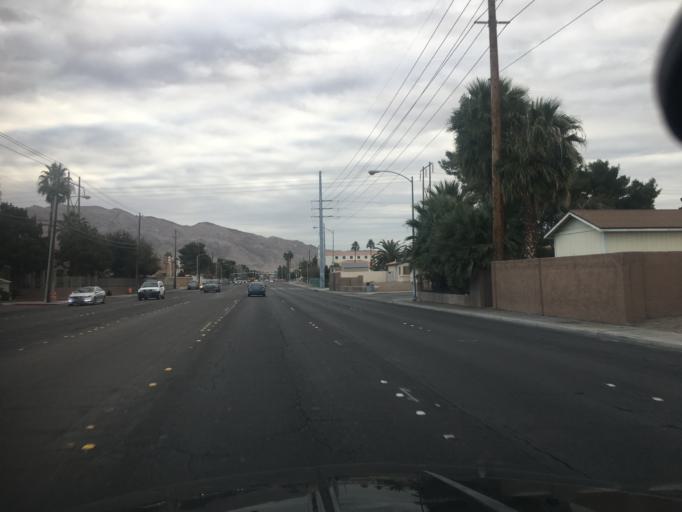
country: US
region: Nevada
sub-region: Clark County
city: Sunrise Manor
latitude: 36.1592
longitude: -115.0577
